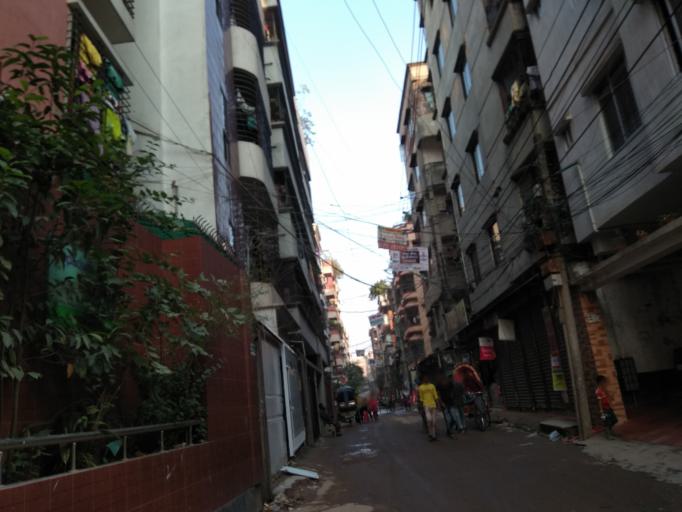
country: BD
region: Dhaka
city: Azimpur
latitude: 23.7594
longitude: 90.3543
